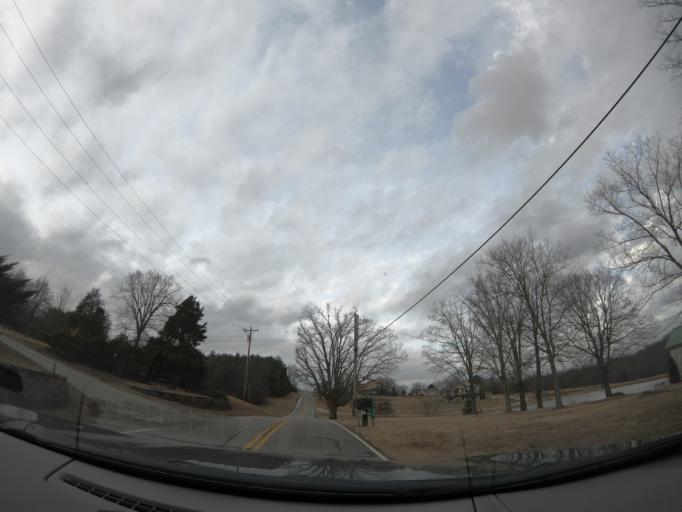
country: US
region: Indiana
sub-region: Floyd County
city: Galena
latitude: 38.3946
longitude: -85.9108
